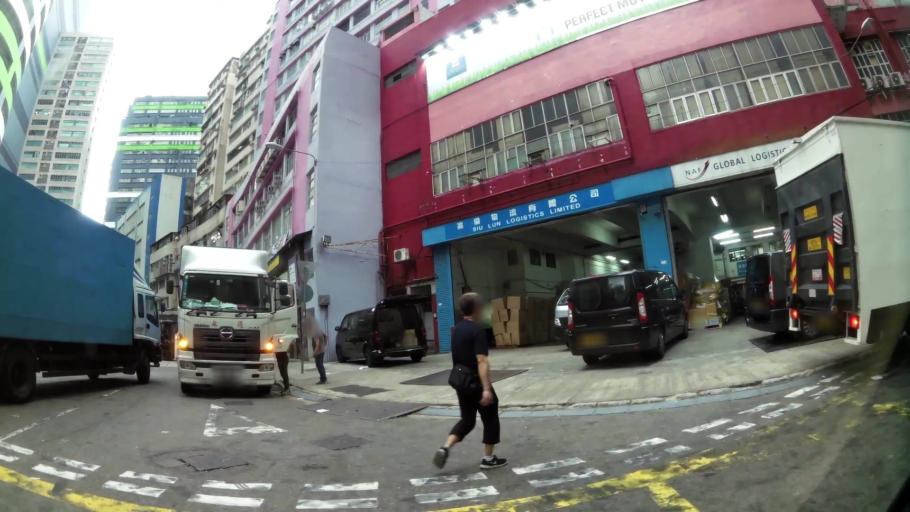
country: HK
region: Tsuen Wan
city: Tsuen Wan
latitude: 22.3657
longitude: 114.1183
